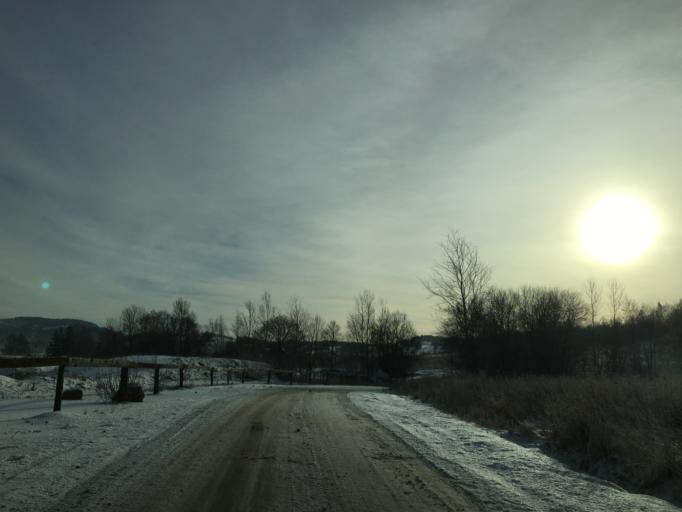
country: PL
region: Lower Silesian Voivodeship
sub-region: Powiat walbrzyski
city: Gluszyca
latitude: 50.6746
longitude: 16.3619
